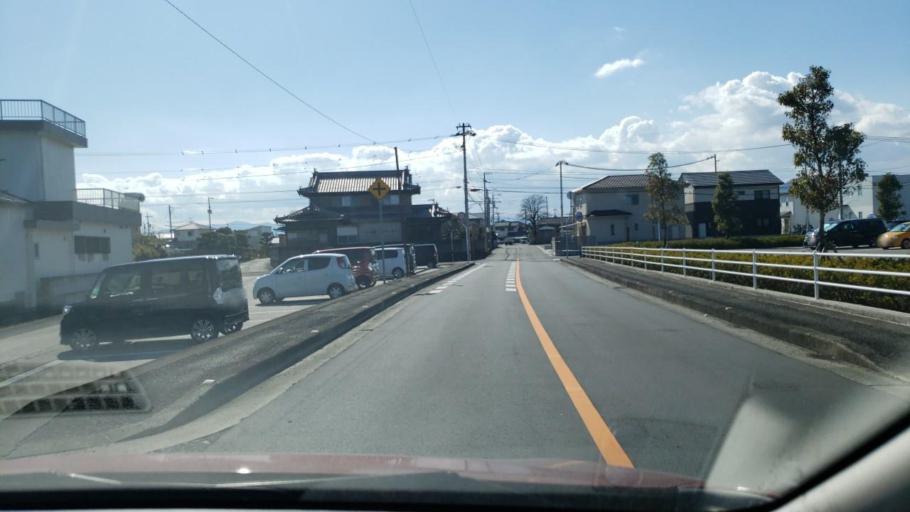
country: JP
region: Tokushima
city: Tokushima-shi
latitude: 34.1329
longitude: 134.5271
